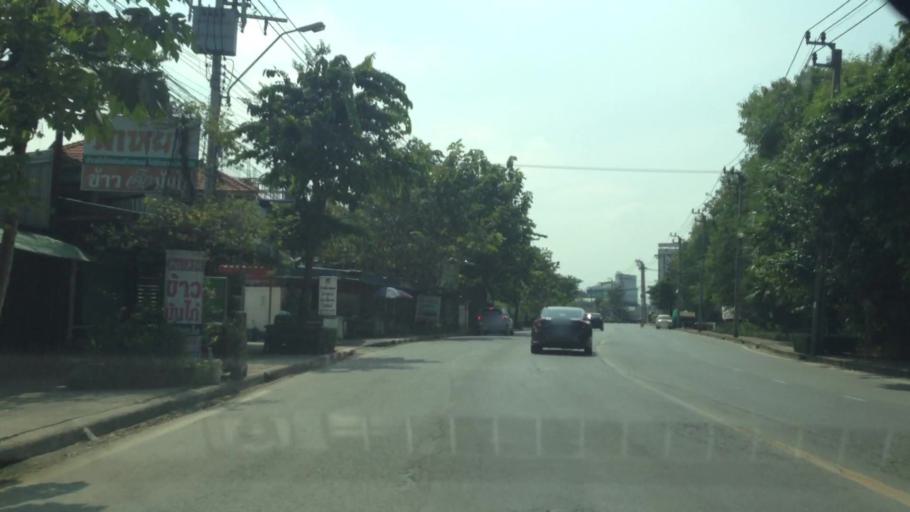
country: TH
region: Bangkok
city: Bang Khen
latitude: 13.8826
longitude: 100.6437
